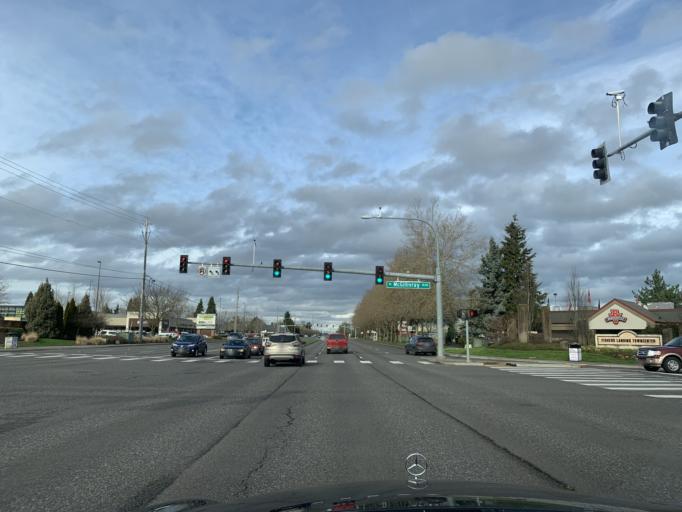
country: US
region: Washington
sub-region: Clark County
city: Mill Plain
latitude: 45.6042
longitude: -122.5038
